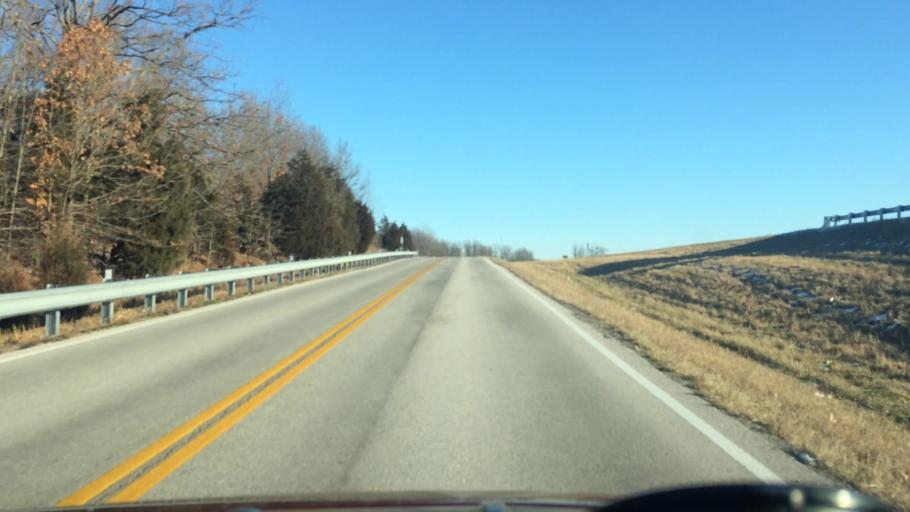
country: US
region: Missouri
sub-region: Greene County
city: Strafford
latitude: 37.2806
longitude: -93.0450
